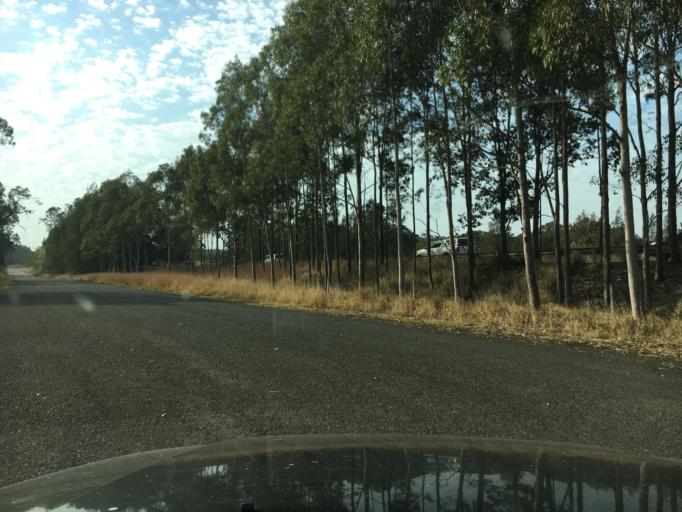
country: AU
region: New South Wales
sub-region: Cessnock
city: Branxton
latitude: -32.6526
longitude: 151.2708
